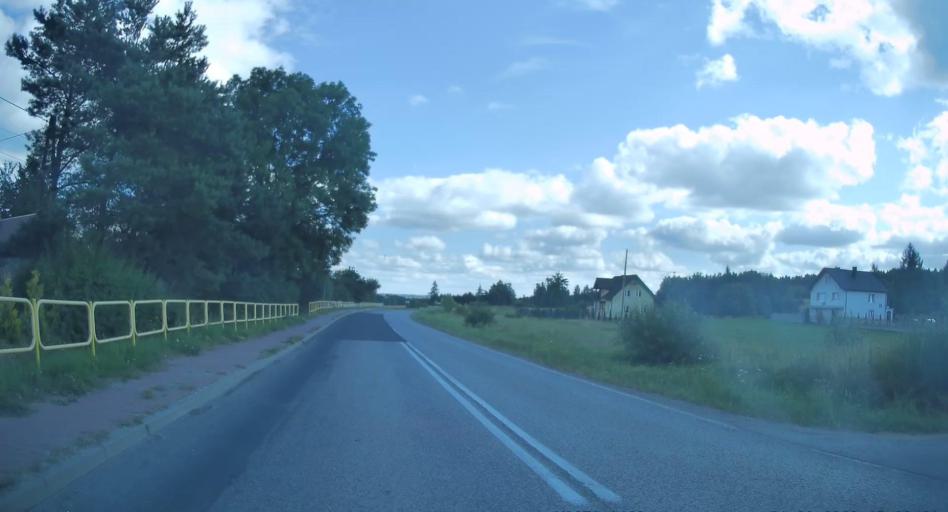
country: PL
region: Swietokrzyskie
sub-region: Powiat kielecki
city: Lagow
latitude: 50.8139
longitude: 21.0786
